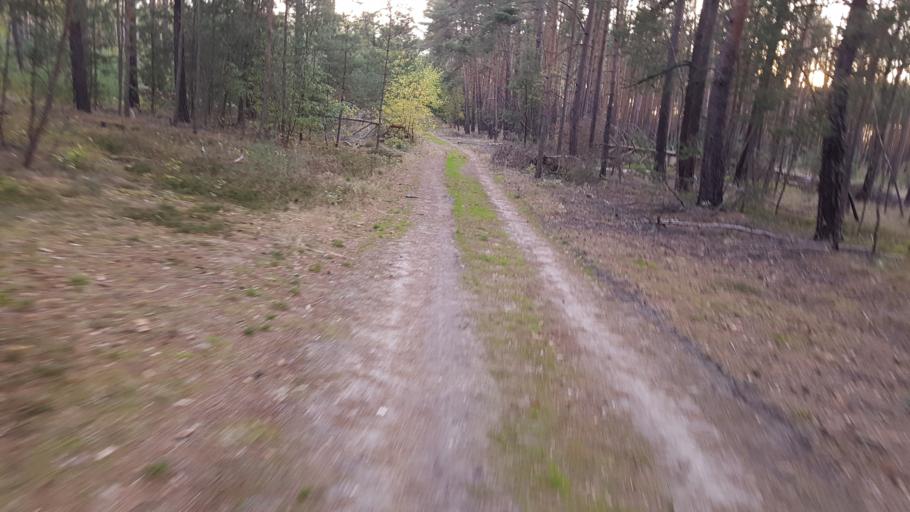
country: DE
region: Brandenburg
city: Bad Liebenwerda
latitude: 51.5484
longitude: 13.4290
